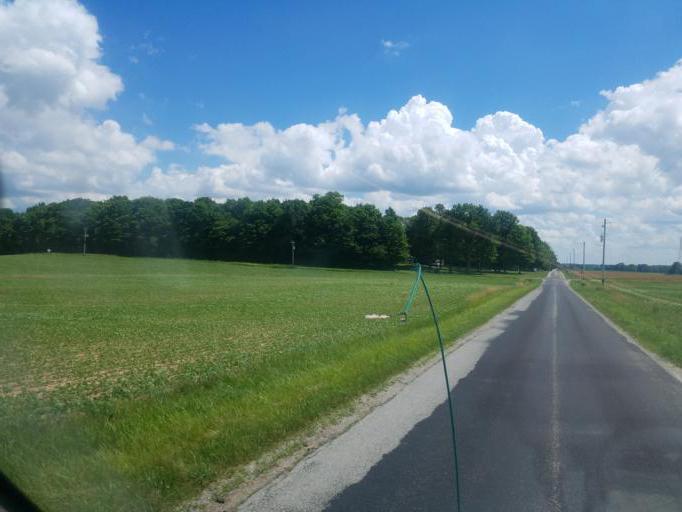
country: US
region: Ohio
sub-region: Crawford County
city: Crestline
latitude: 40.8592
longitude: -82.8371
